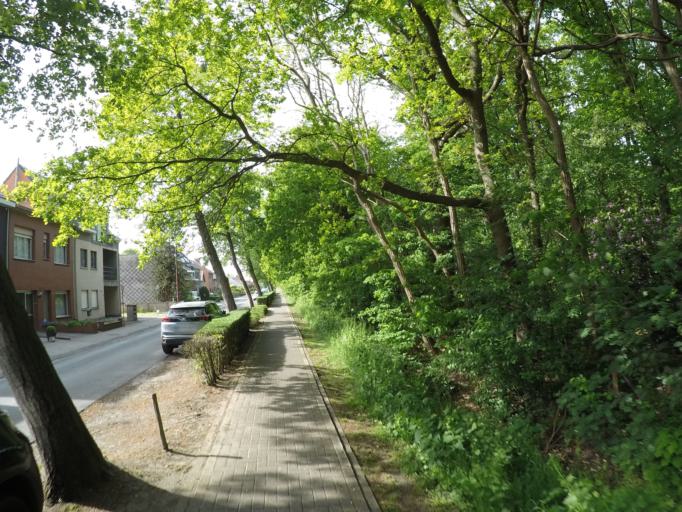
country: BE
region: Flanders
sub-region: Provincie Antwerpen
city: Kapellen
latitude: 51.3135
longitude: 4.4088
